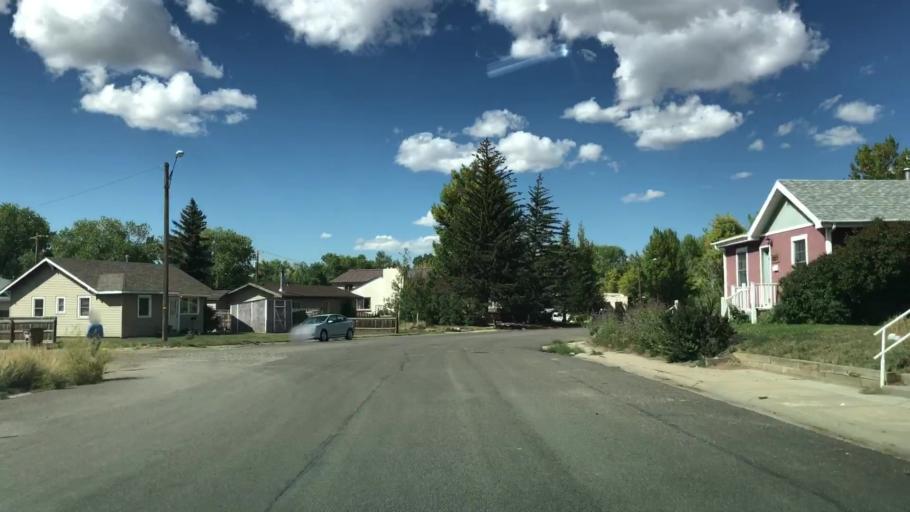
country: US
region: Wyoming
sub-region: Albany County
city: Laramie
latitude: 41.3012
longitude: -105.5918
